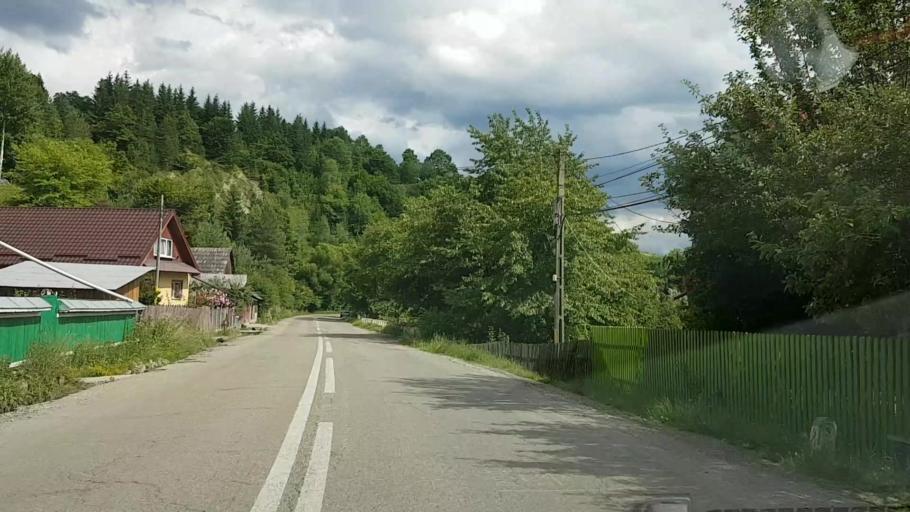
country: RO
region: Neamt
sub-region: Comuna Hangu
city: Hangu
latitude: 47.0292
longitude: 26.0662
